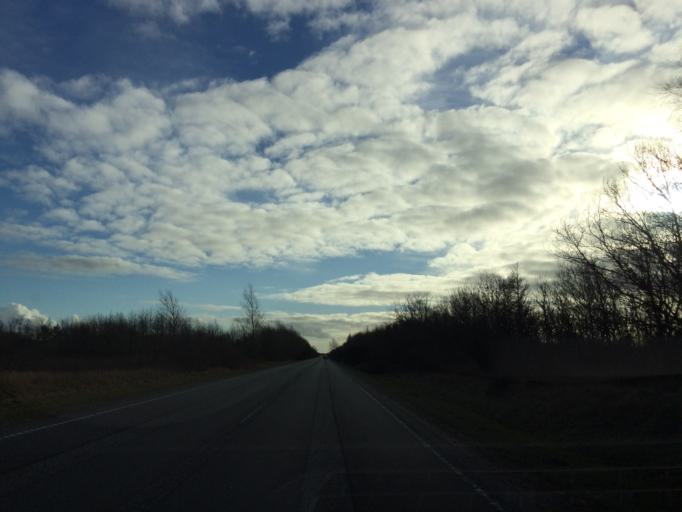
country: DK
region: Central Jutland
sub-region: Lemvig Kommune
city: Lemvig
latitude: 56.5029
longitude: 8.3027
